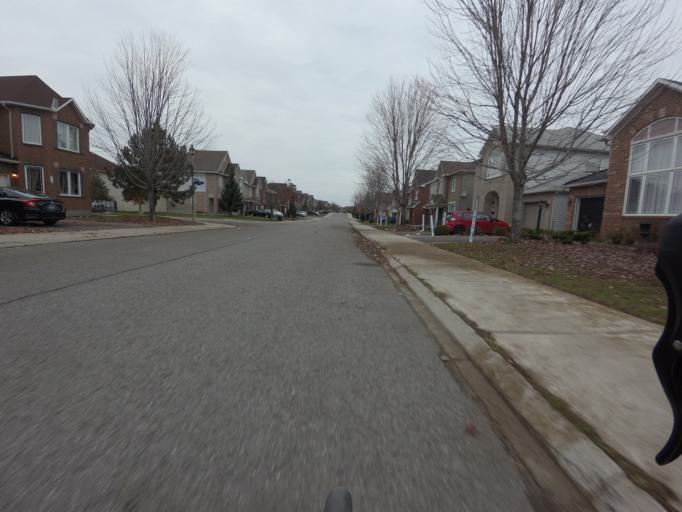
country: CA
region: Ontario
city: Bells Corners
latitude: 45.2747
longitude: -75.7068
